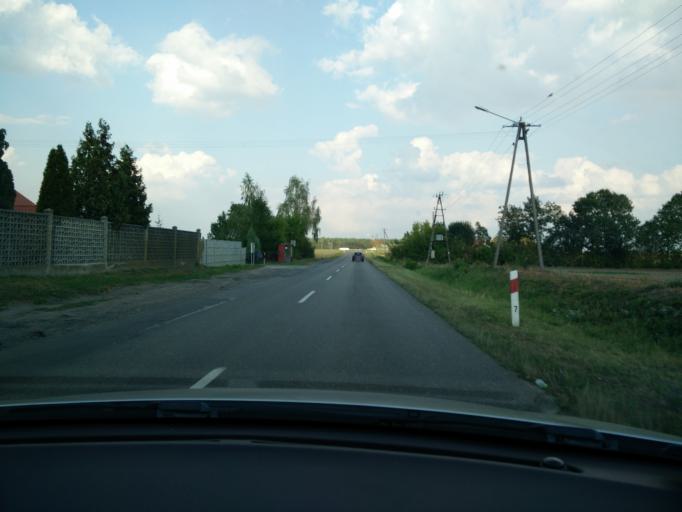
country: PL
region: Greater Poland Voivodeship
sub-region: Powiat sredzki
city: Dominowo
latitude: 52.2375
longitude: 17.3349
